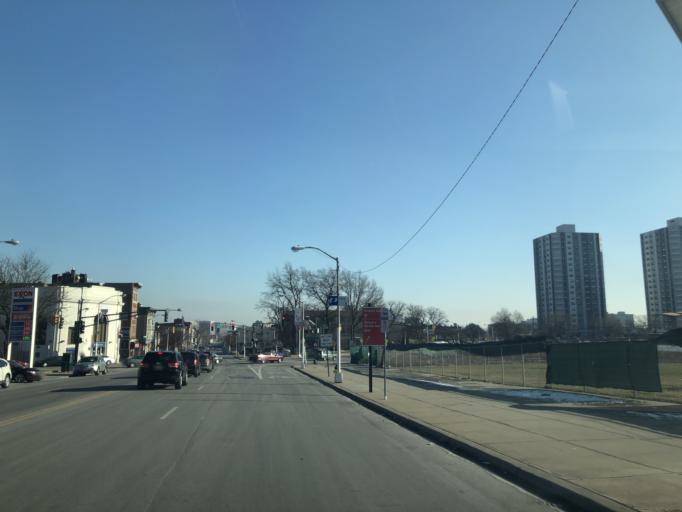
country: US
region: New Jersey
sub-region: Essex County
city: East Orange
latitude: 40.7482
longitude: -74.1938
